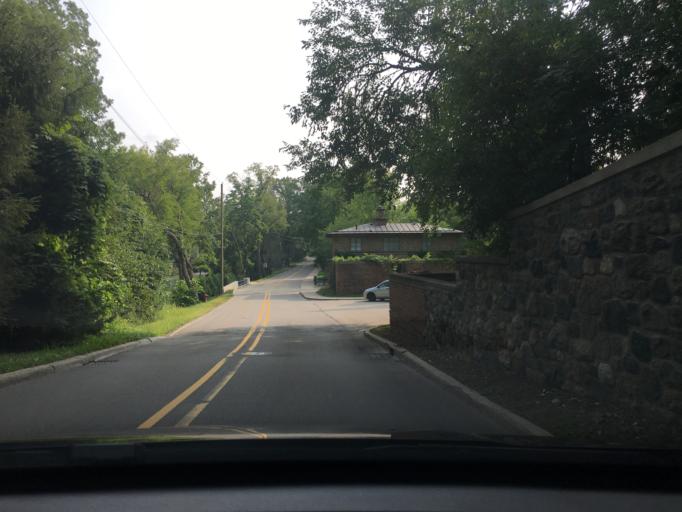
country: US
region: Michigan
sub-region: Oakland County
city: Bloomfield Hills
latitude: 42.5732
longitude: -83.2418
